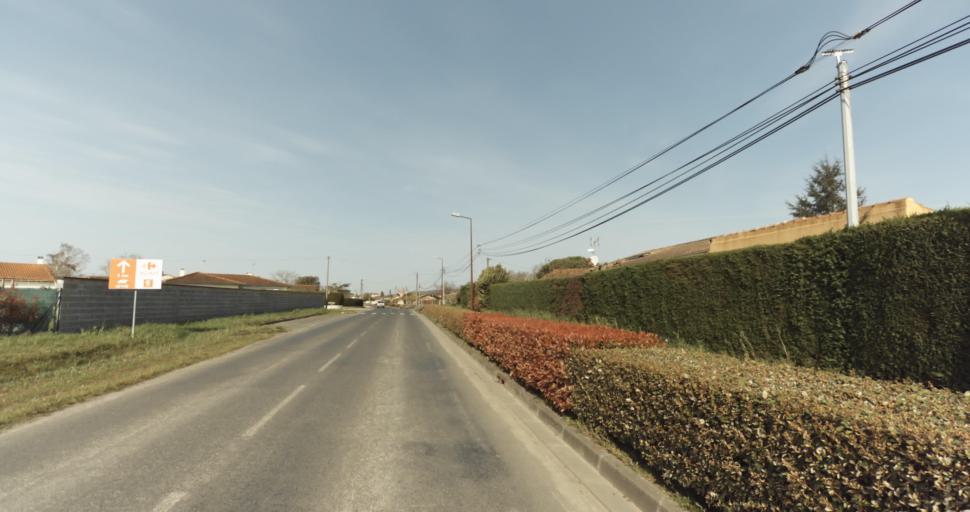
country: FR
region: Midi-Pyrenees
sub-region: Departement du Tarn
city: Saint-Sulpice-la-Pointe
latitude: 43.7717
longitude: 1.6990
